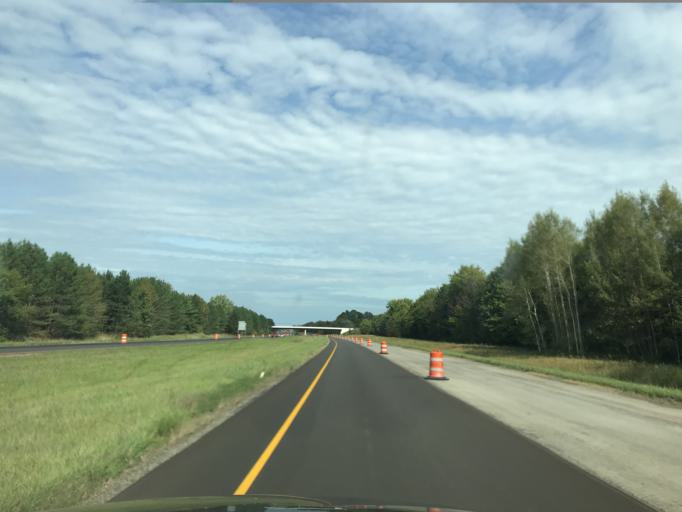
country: US
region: Ohio
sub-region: Ashtabula County
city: Jefferson
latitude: 41.7187
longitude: -80.7070
